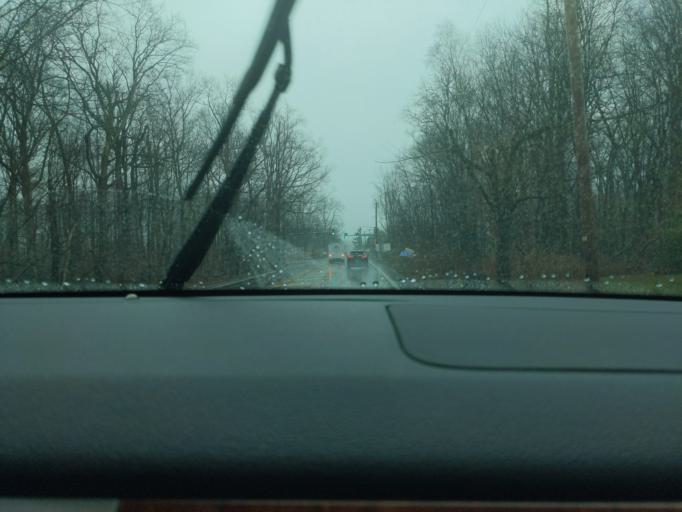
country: US
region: Pennsylvania
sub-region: Bucks County
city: Perkasie
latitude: 40.4217
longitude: -75.2779
